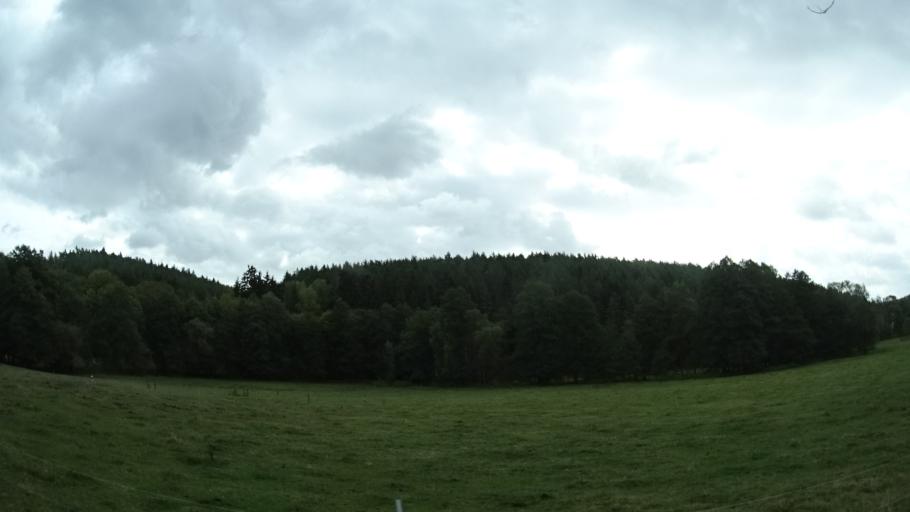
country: DE
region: Thuringia
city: Mehmels
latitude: 50.6430
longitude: 10.3422
